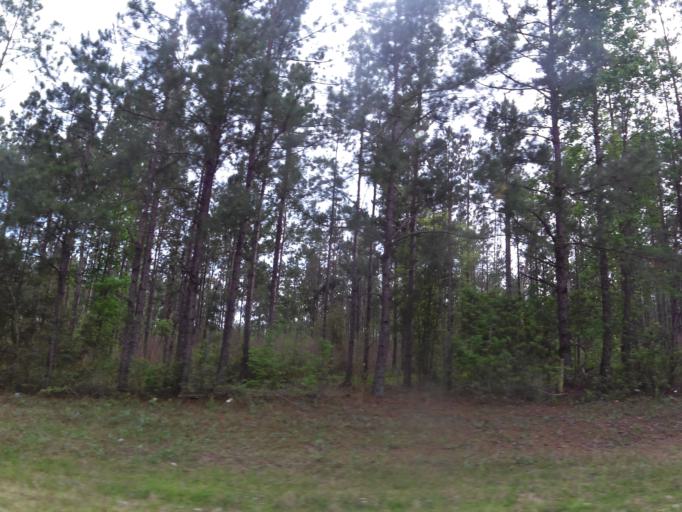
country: US
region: Florida
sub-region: Nassau County
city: Hilliard
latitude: 30.6950
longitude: -81.8594
